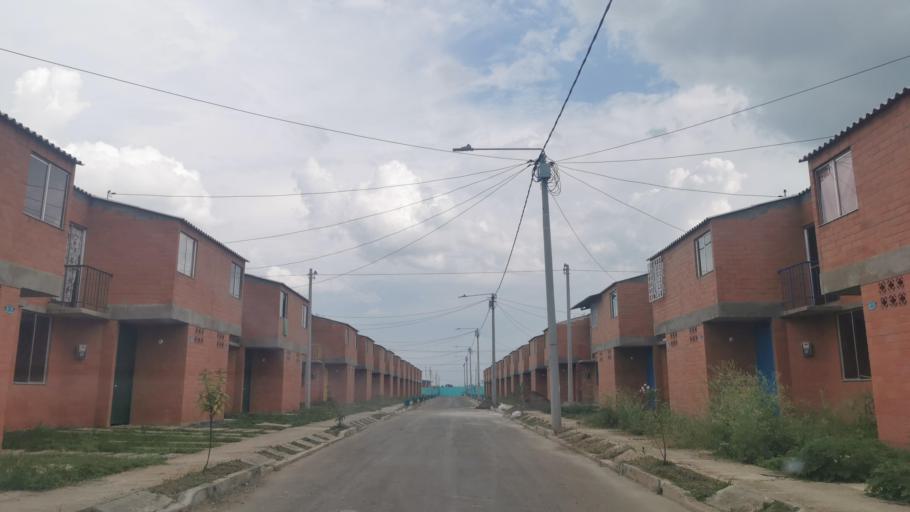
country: CO
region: Valle del Cauca
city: Jamundi
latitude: 3.2325
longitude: -76.5255
